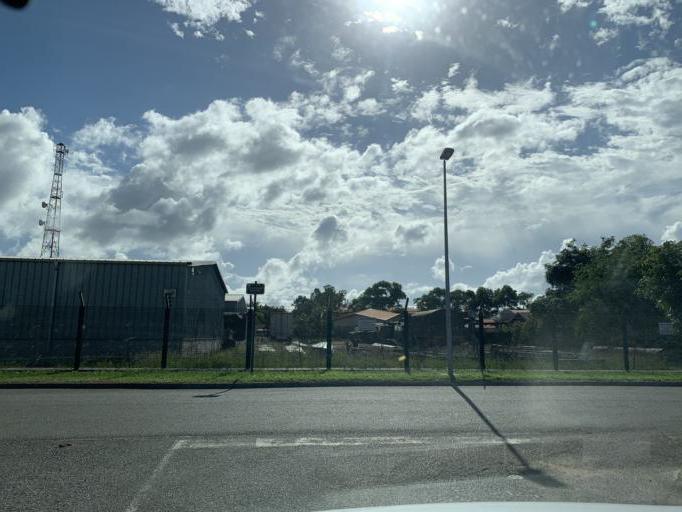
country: GF
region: Guyane
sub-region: Guyane
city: Kourou
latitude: 5.1727
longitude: -52.6467
